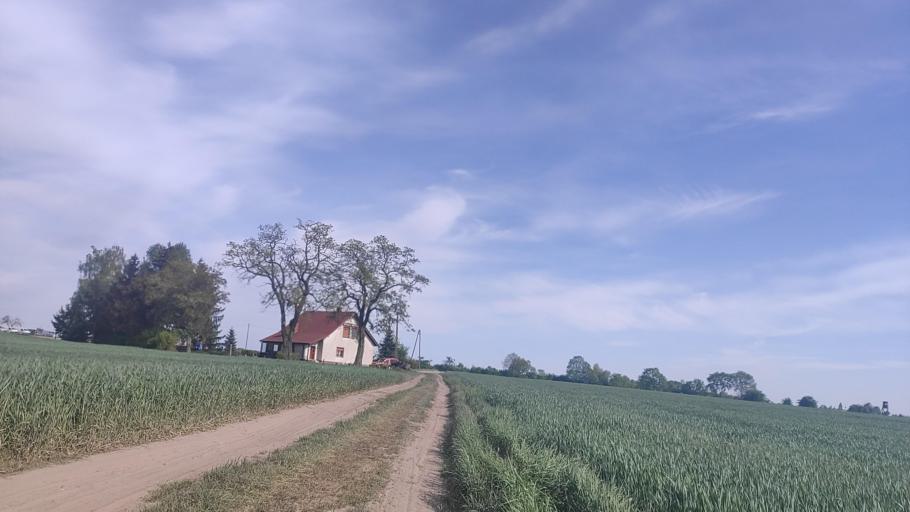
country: PL
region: Greater Poland Voivodeship
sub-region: Powiat poznanski
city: Swarzedz
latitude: 52.4148
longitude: 17.1513
